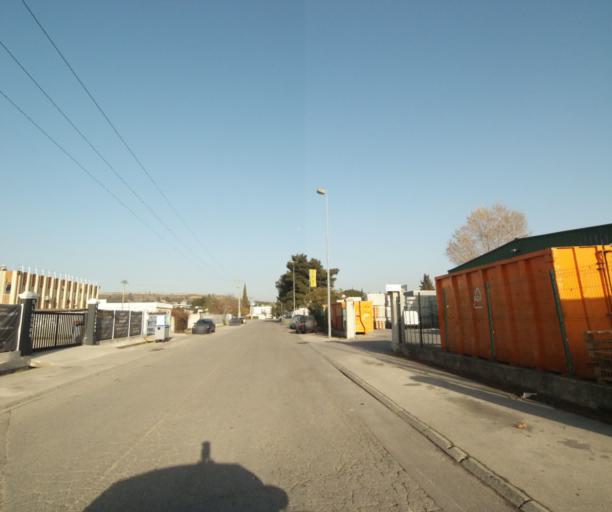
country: FR
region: Provence-Alpes-Cote d'Azur
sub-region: Departement des Bouches-du-Rhone
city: Saint-Victoret
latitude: 43.4263
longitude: 5.2552
